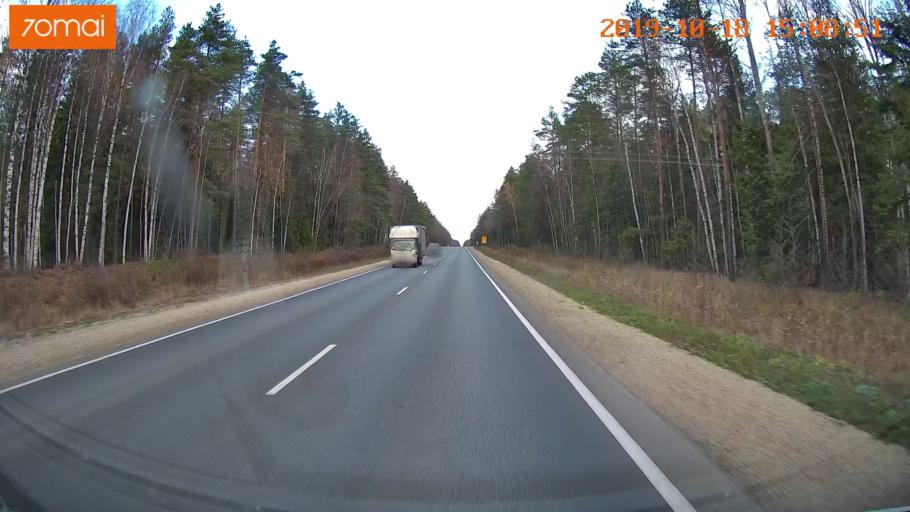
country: RU
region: Vladimir
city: Gus'-Khrustal'nyy
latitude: 55.5579
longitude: 40.6148
